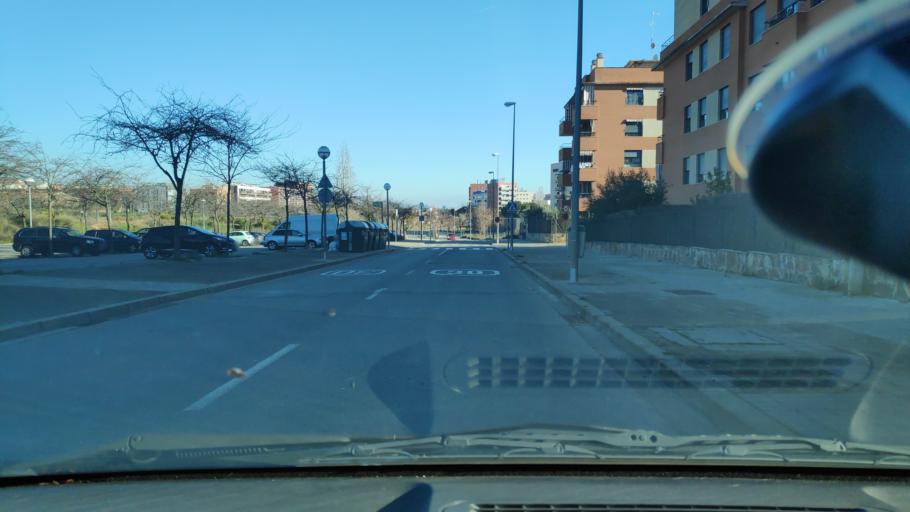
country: ES
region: Catalonia
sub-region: Provincia de Barcelona
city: Sant Quirze del Valles
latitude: 41.5635
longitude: 2.0757
